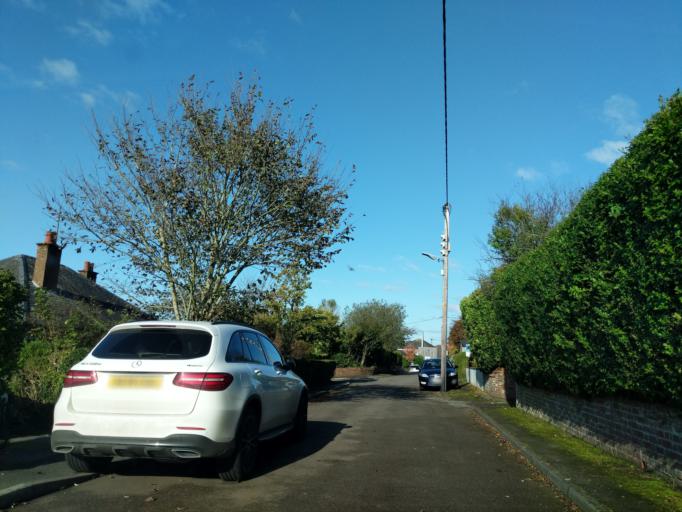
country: GB
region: Scotland
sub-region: Dumfries and Galloway
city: Kirkcudbright
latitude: 54.8335
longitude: -4.0508
